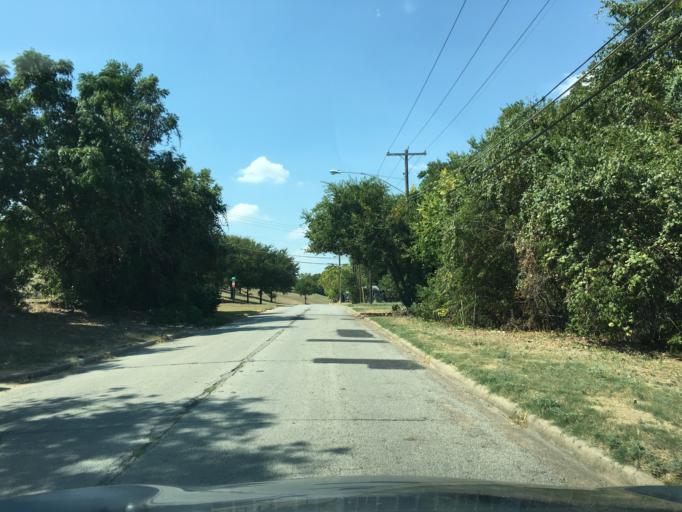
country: US
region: Texas
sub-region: Dallas County
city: Dallas
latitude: 32.7526
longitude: -96.8048
